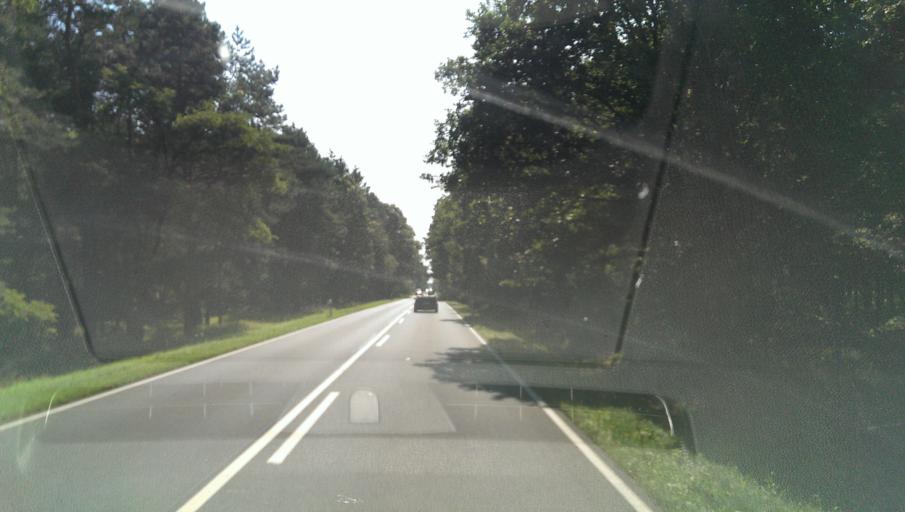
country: DE
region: Saxony-Anhalt
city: Abtsdorf
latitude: 51.9246
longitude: 12.7022
